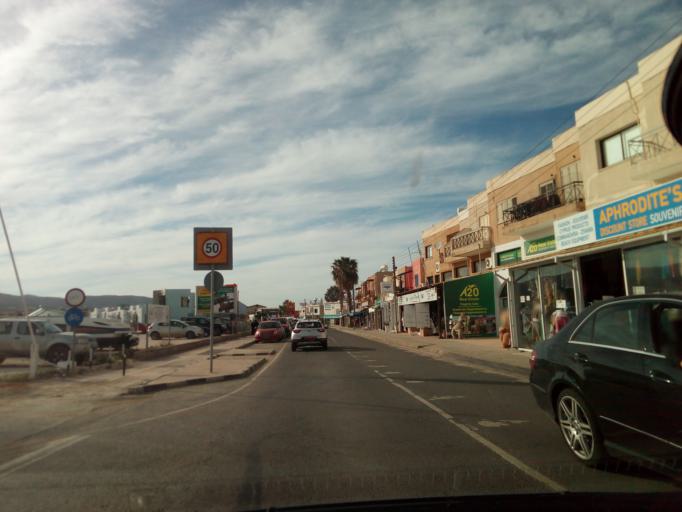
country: CY
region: Pafos
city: Polis
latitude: 35.0397
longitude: 32.3966
